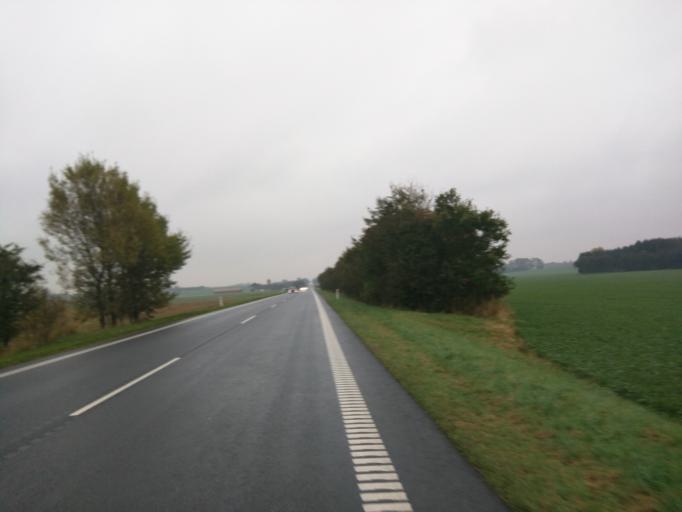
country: DK
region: Central Jutland
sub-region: Silkeborg Kommune
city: Kjellerup
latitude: 56.3684
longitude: 9.4391
